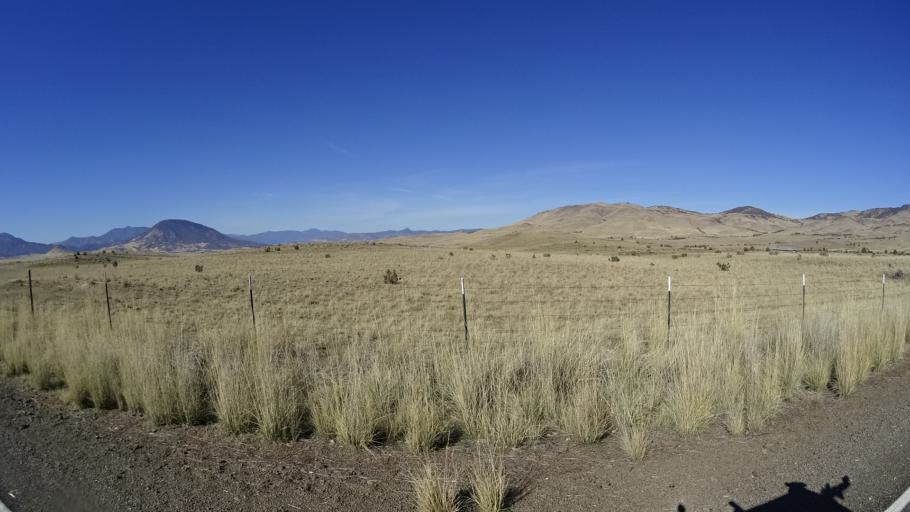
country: US
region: California
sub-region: Siskiyou County
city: Montague
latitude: 41.8058
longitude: -122.3916
